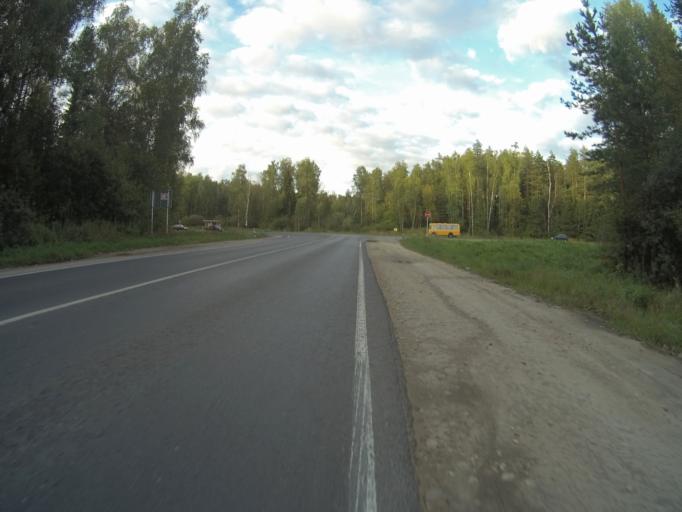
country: RU
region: Vladimir
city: Kommunar
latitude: 56.0183
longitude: 40.5809
